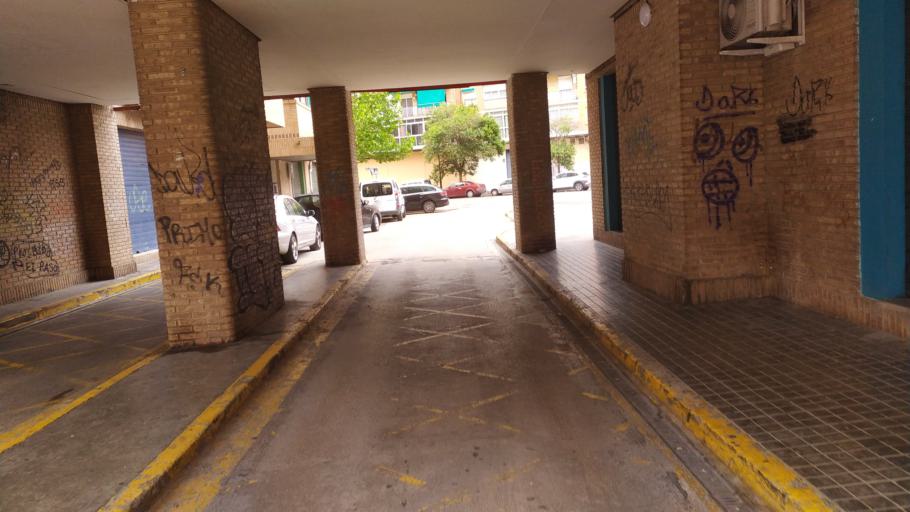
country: ES
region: Valencia
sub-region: Provincia de Valencia
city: Mislata
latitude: 39.4681
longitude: -0.4171
